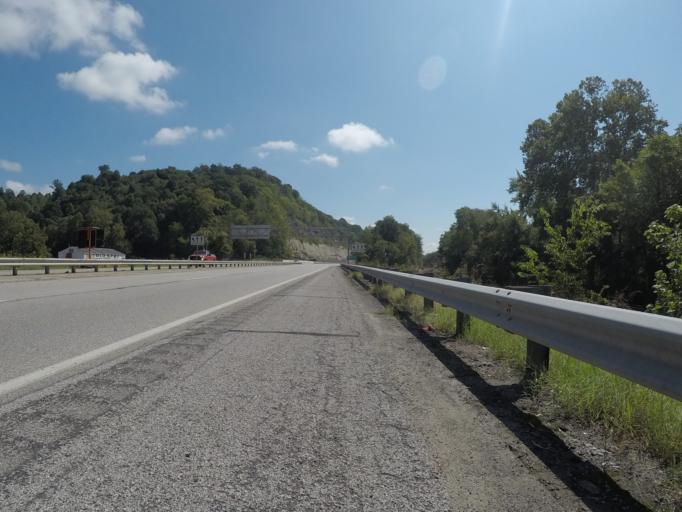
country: US
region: Kentucky
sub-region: Boyd County
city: Ashland
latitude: 38.4809
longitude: -82.6242
